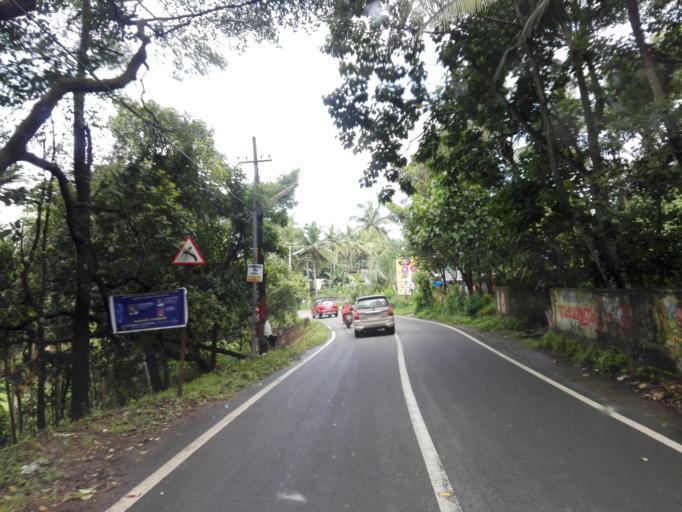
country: IN
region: Kerala
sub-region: Ernakulam
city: Aluva
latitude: 10.0266
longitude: 76.3684
